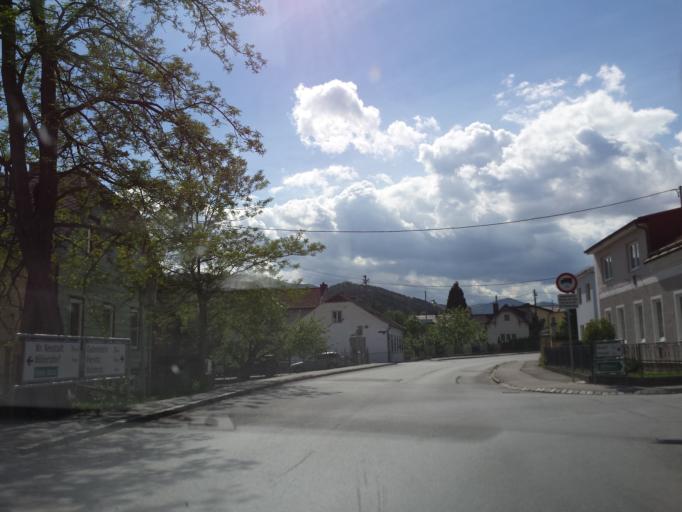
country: AT
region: Lower Austria
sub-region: Politischer Bezirk Wiener Neustadt
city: Markt Piesting
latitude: 47.8728
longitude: 16.1219
